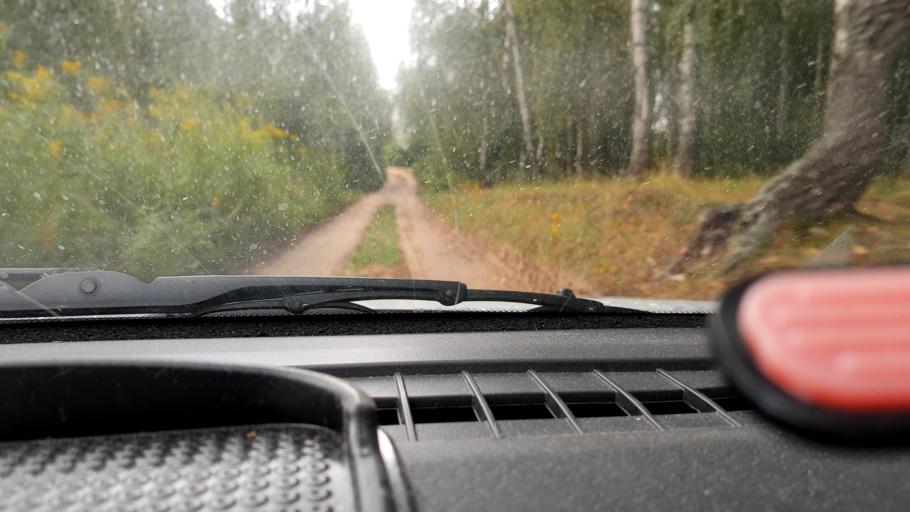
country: RU
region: Nizjnij Novgorod
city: Afonino
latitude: 56.3212
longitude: 44.1601
